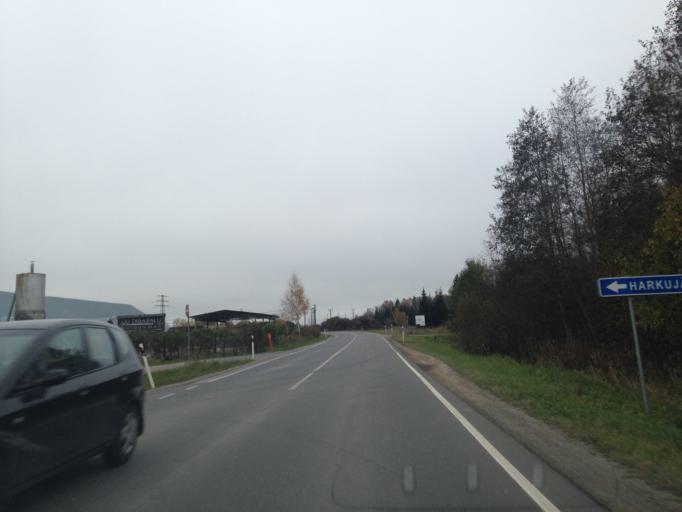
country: EE
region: Harju
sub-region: Harku vald
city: Tabasalu
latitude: 59.4162
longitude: 24.5437
